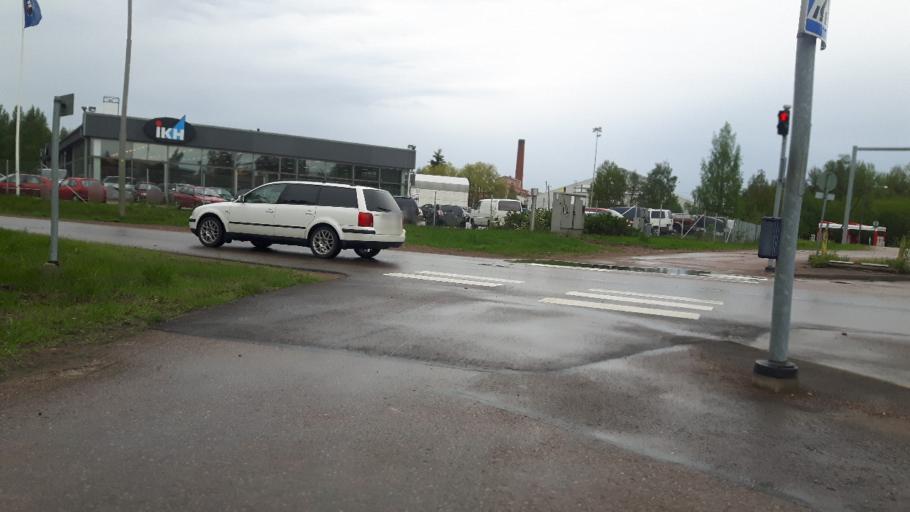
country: FI
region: Kymenlaakso
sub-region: Kotka-Hamina
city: Kotka
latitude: 60.4962
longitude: 26.9004
